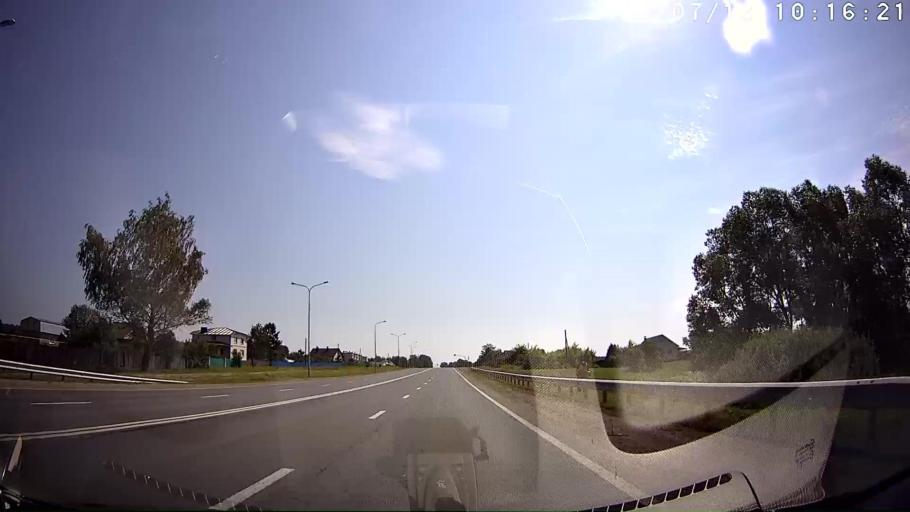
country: RU
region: Mariy-El
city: Sovetskiy
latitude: 56.7468
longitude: 48.3366
